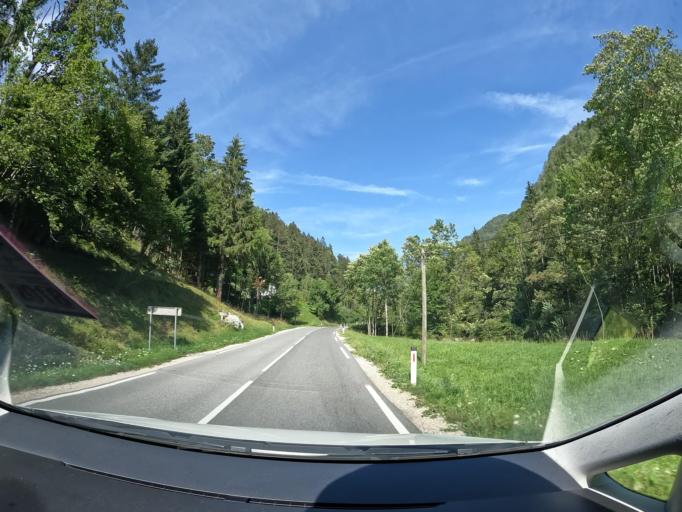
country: SI
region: Zirovnica
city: Zirovnica
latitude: 46.4398
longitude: 14.1950
